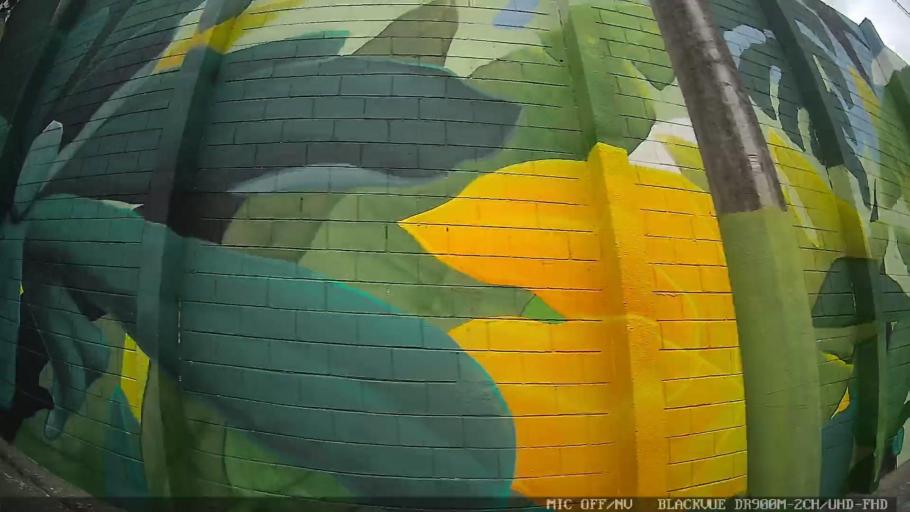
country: BR
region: Sao Paulo
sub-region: Guaruja
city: Guaruja
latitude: -23.9905
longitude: -46.2658
